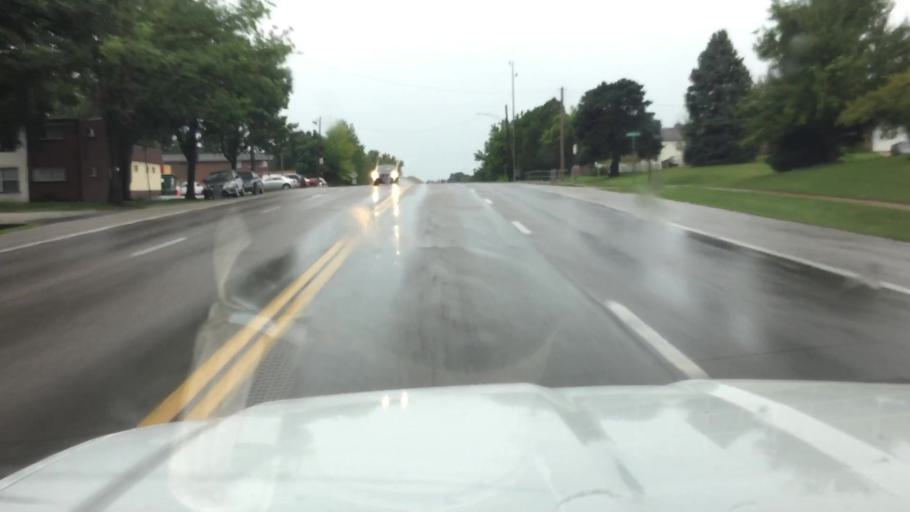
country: US
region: Missouri
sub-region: Saint Louis County
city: Lemay
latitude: 38.5189
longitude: -90.2810
